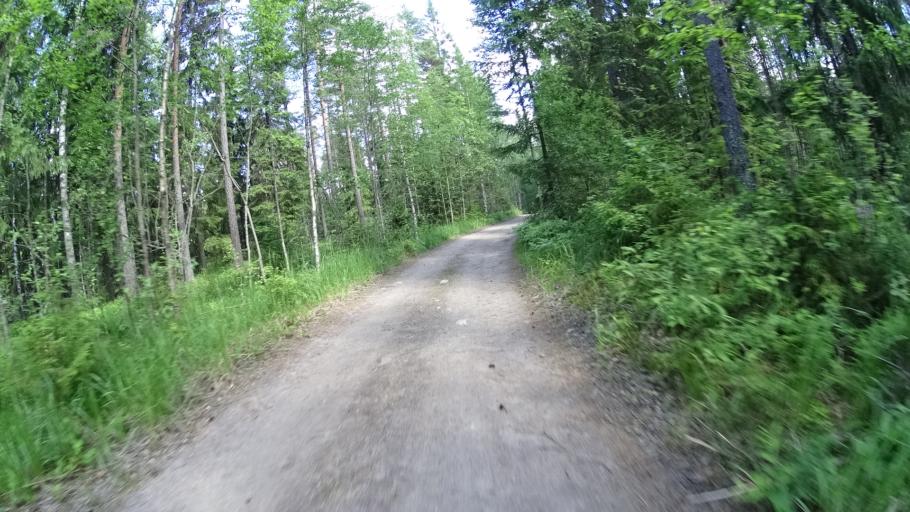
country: FI
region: Uusimaa
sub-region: Helsinki
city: Vihti
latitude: 60.3266
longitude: 24.4601
